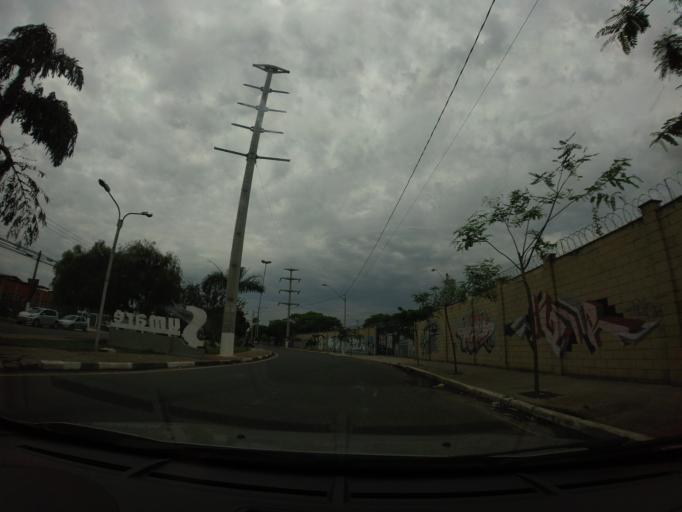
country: BR
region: Sao Paulo
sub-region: Hortolandia
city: Hortolandia
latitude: -22.8414
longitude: -47.1586
